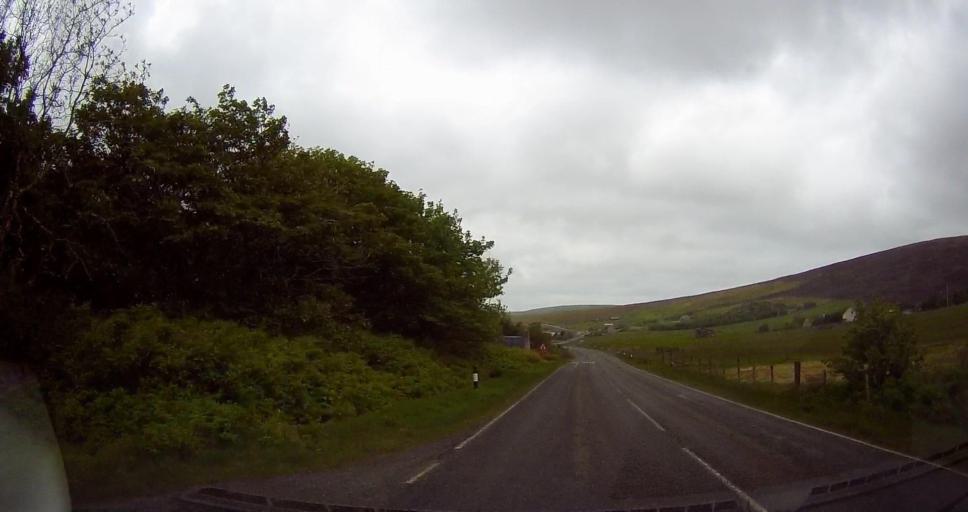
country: GB
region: Scotland
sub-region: Shetland Islands
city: Lerwick
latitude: 60.2421
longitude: -1.3438
